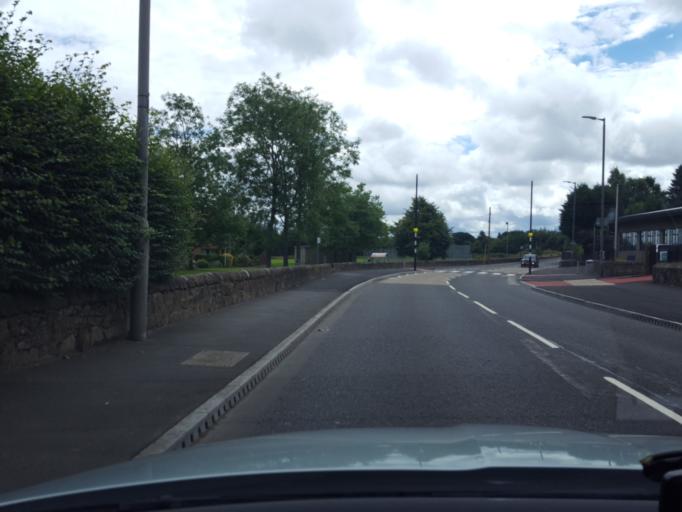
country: GB
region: Scotland
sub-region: Stirling
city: Plean
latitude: 56.0627
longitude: -3.8725
